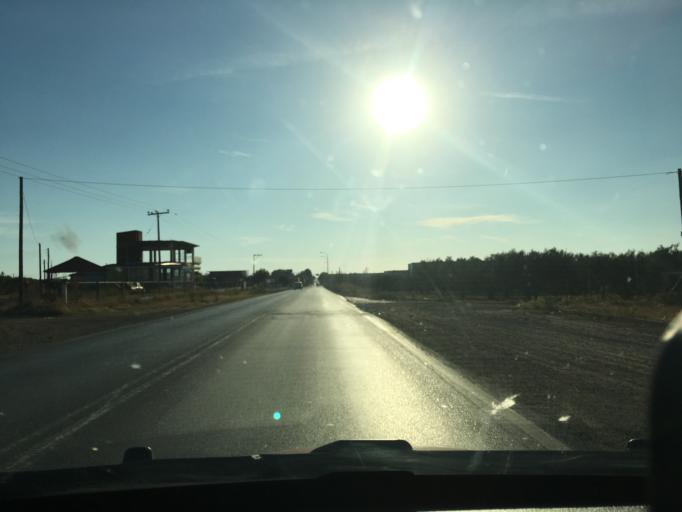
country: GR
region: Central Macedonia
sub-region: Nomos Chalkidikis
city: Nea Moudhania
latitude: 40.2534
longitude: 23.3195
